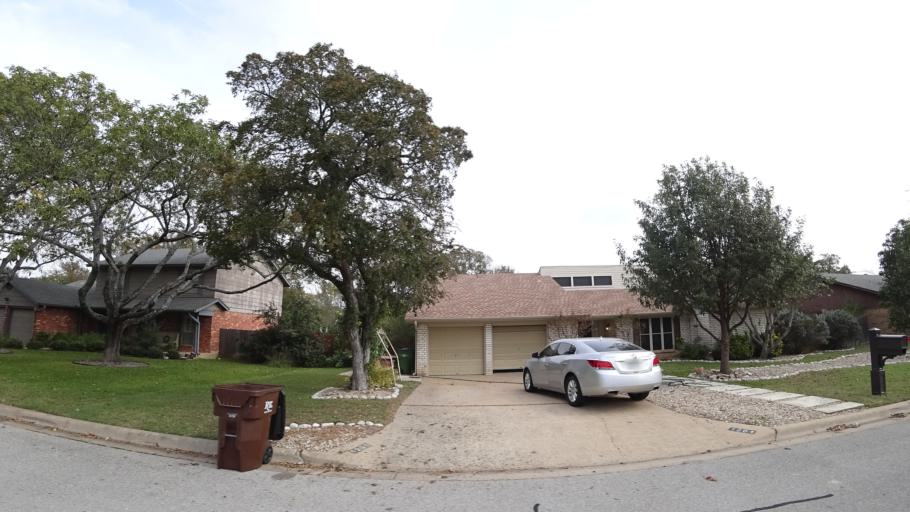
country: US
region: Texas
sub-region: Williamson County
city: Round Rock
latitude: 30.4976
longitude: -97.6899
